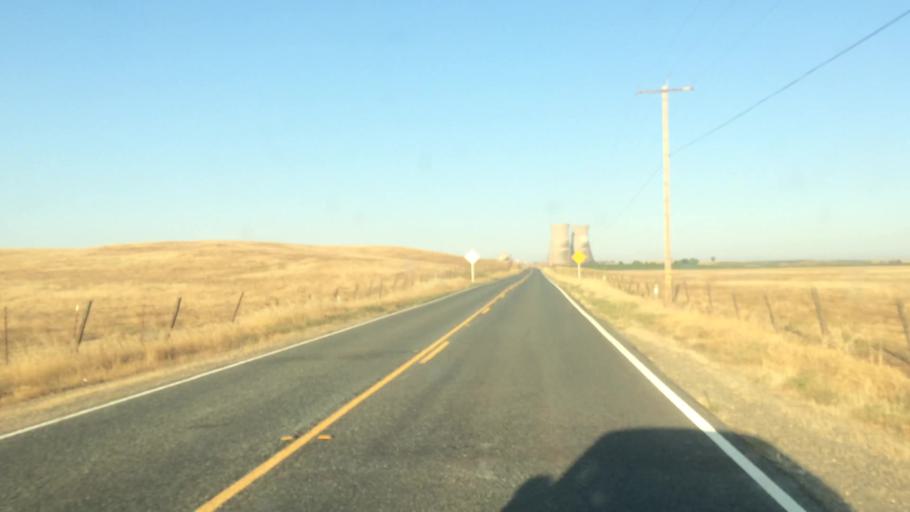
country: US
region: California
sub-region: Sacramento County
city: Clay
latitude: 38.3503
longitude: -121.0970
